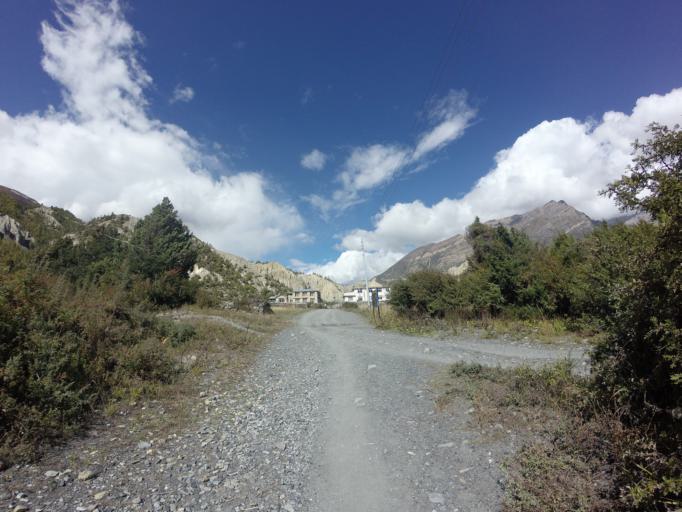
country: NP
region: Western Region
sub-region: Gandaki Zone
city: Nawal
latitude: 28.6372
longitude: 84.0924
